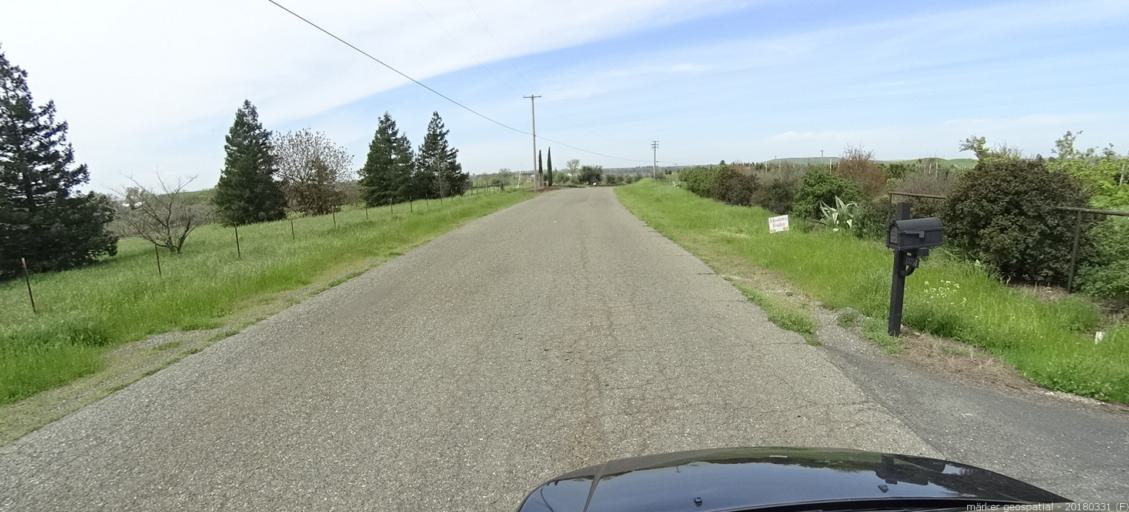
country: US
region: California
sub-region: Sacramento County
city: Rancho Murieta
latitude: 38.4916
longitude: -121.1457
